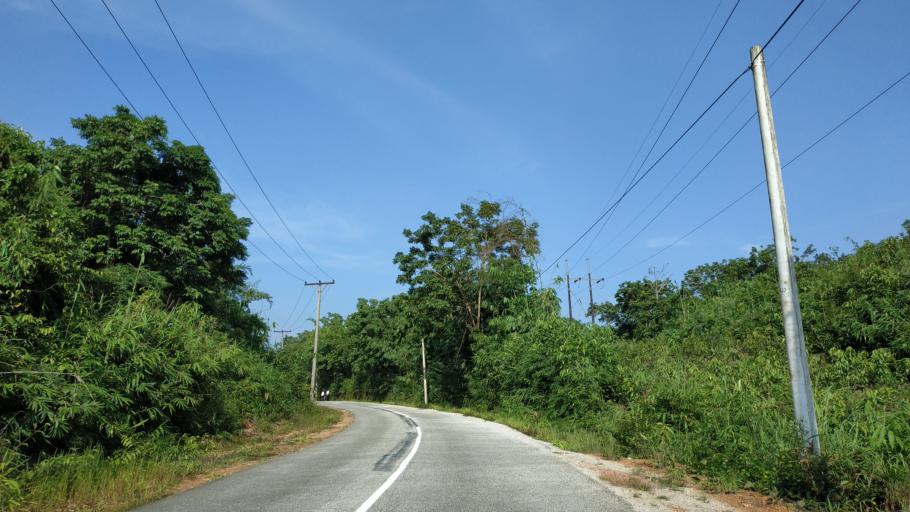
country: TH
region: Kanchanaburi
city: Thong Pha Phum
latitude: 14.6269
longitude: 98.1217
